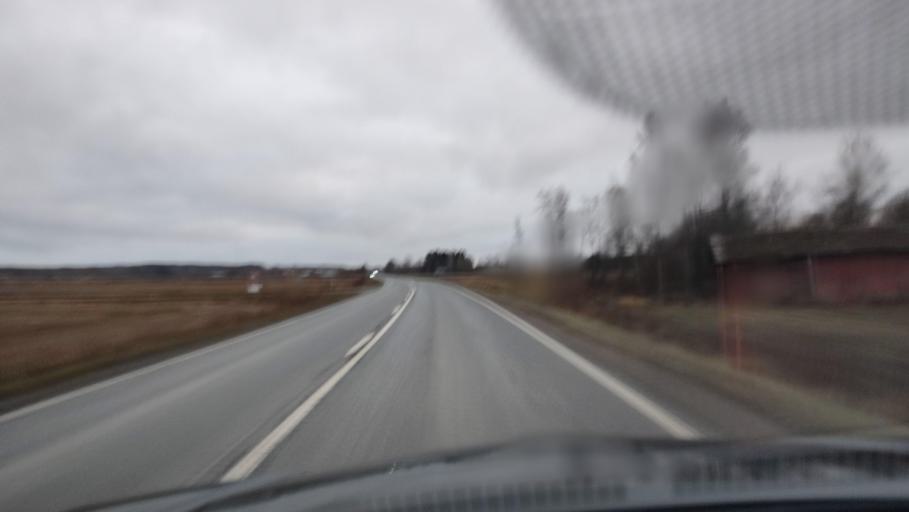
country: FI
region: Southern Ostrobothnia
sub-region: Suupohja
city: Kauhajoki
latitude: 62.3720
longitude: 22.0790
